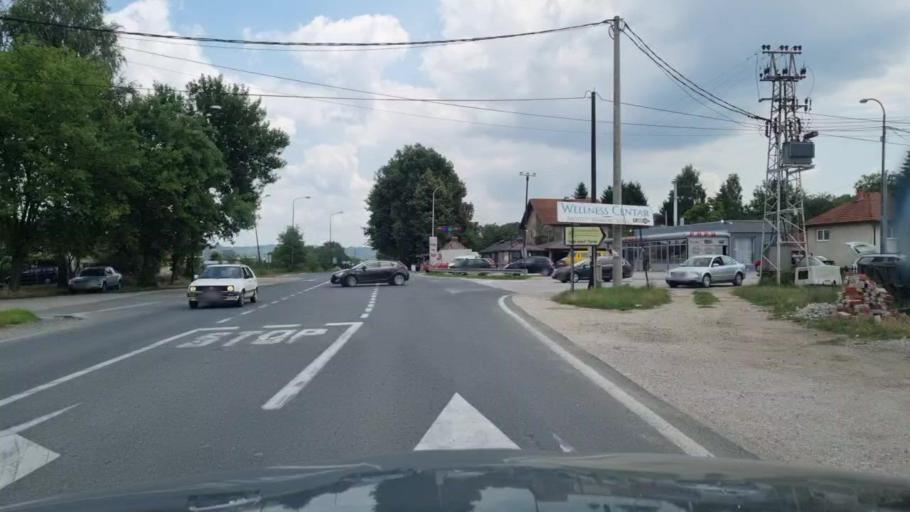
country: BA
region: Federation of Bosnia and Herzegovina
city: Puracic
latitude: 44.5485
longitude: 18.4787
